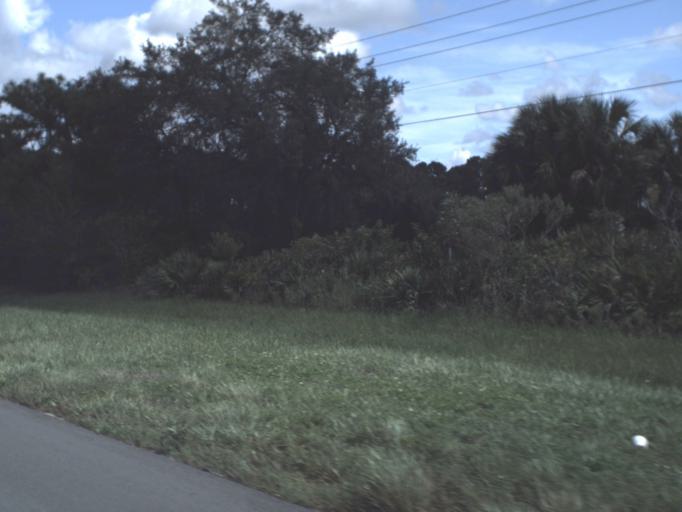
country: US
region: Florida
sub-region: Sarasota County
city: The Meadows
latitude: 27.3528
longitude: -82.4462
